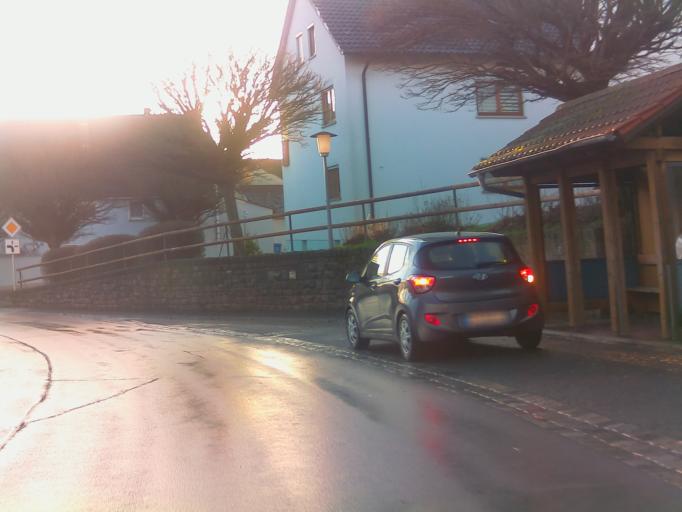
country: DE
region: Bavaria
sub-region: Regierungsbezirk Unterfranken
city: Sondheim vor der Rhoen
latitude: 50.4791
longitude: 10.1811
